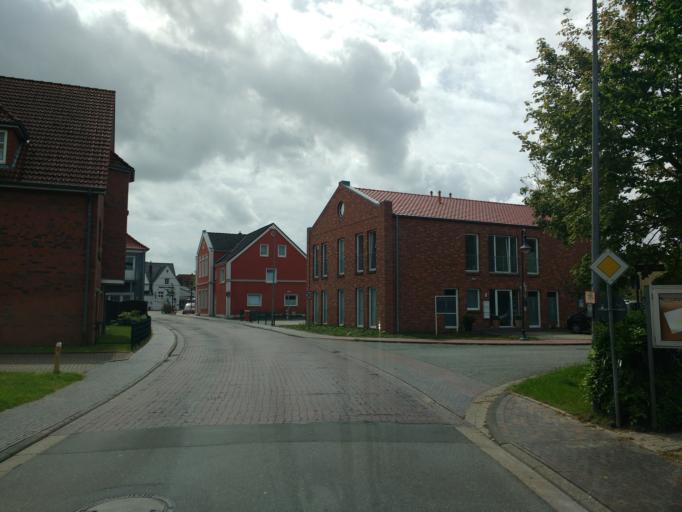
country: DE
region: Lower Saxony
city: Jever
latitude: 53.5769
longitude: 7.9047
